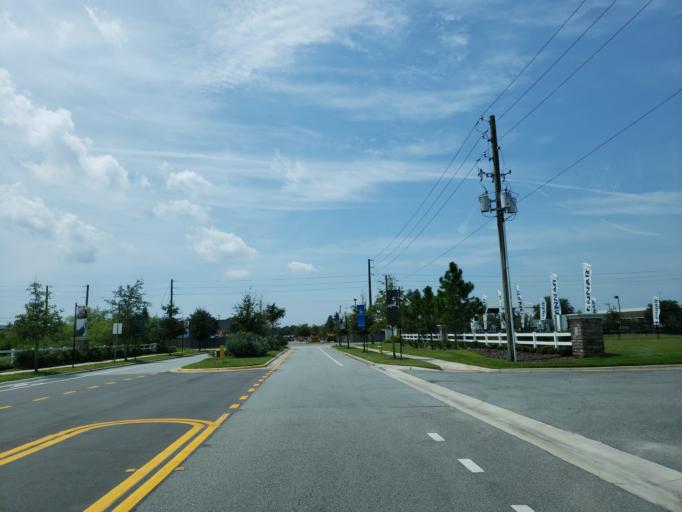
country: US
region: Florida
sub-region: Hillsborough County
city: Riverview
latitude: 27.8463
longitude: -82.3422
